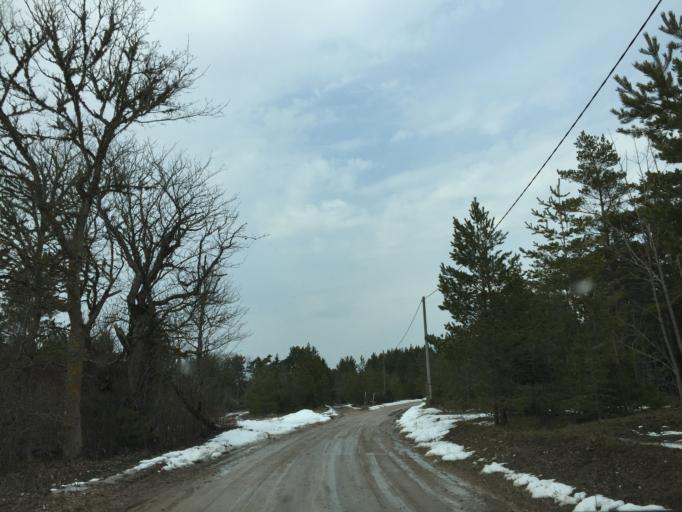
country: EE
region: Saare
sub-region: Kuressaare linn
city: Kuressaare
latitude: 58.4279
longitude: 22.1450
